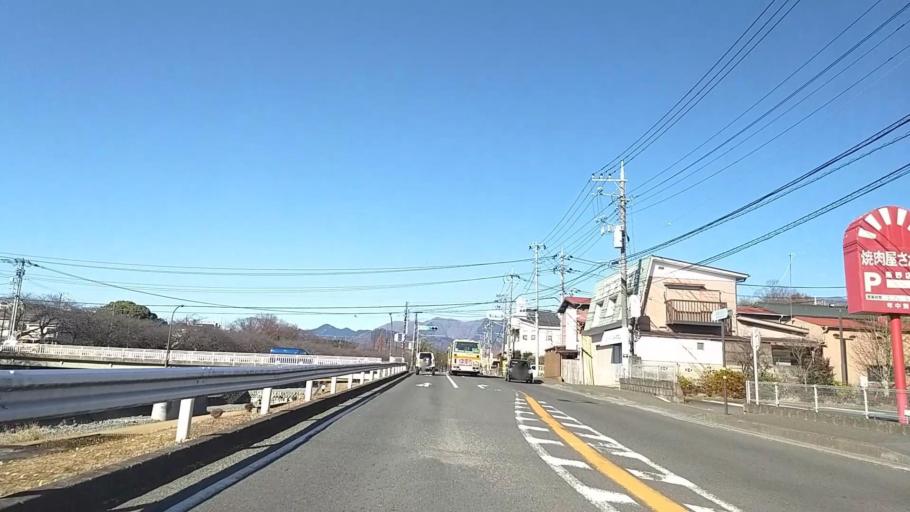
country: JP
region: Kanagawa
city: Hadano
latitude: 35.3777
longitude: 139.2095
